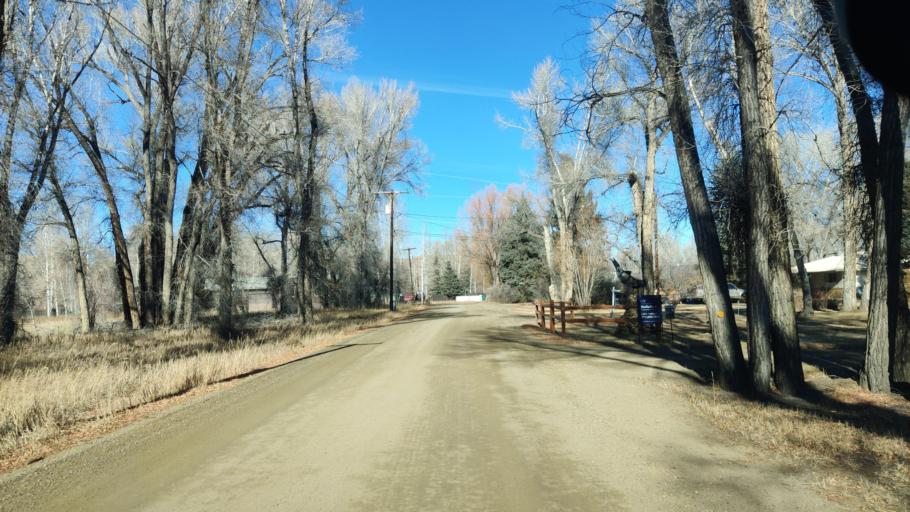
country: US
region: Colorado
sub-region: Gunnison County
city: Gunnison
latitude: 38.5362
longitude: -106.9499
